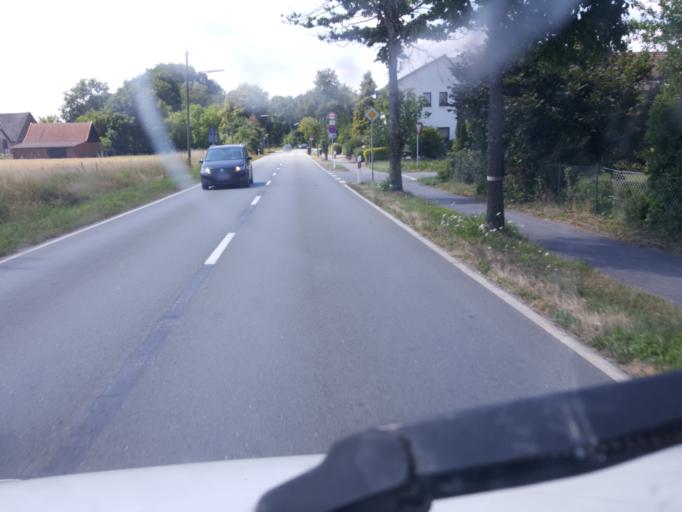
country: DE
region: North Rhine-Westphalia
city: Loehne
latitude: 52.2231
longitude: 8.7289
